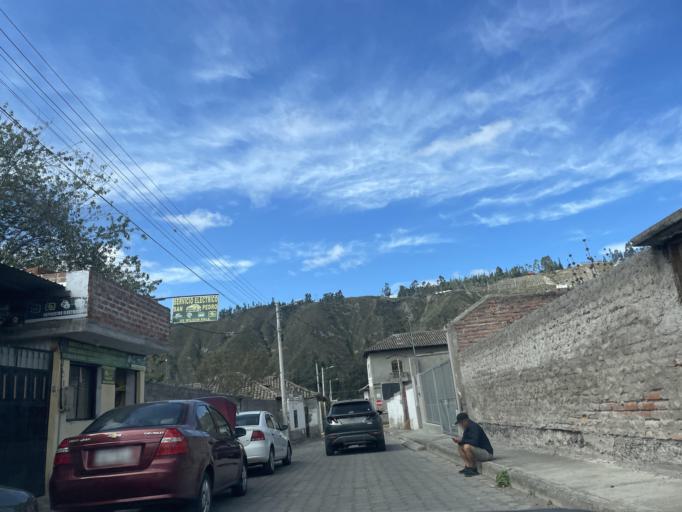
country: EC
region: Chimborazo
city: Guano
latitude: -1.6070
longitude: -78.6397
